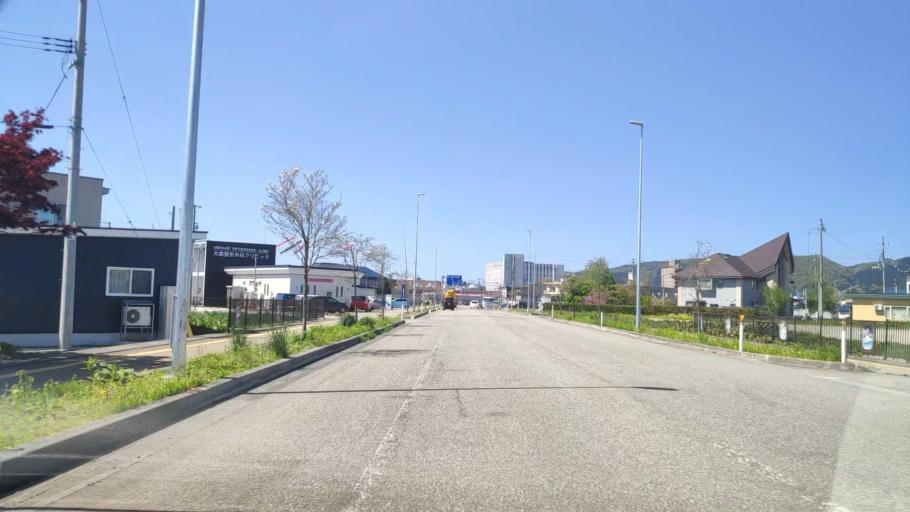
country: JP
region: Akita
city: Omagari
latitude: 39.4682
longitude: 140.4823
